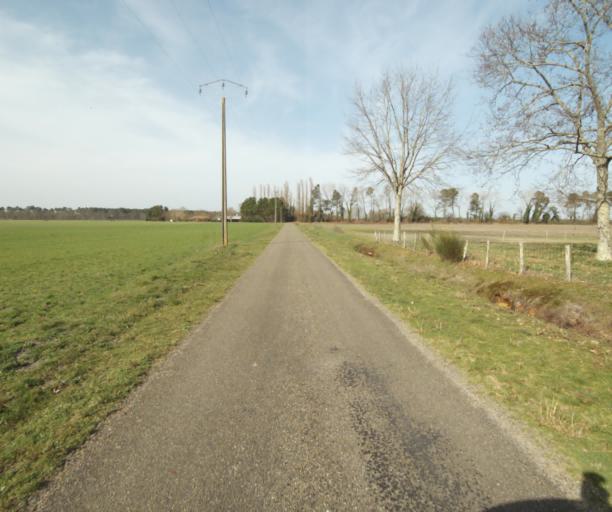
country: FR
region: Aquitaine
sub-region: Departement des Landes
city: Roquefort
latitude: 44.1495
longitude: -0.1623
